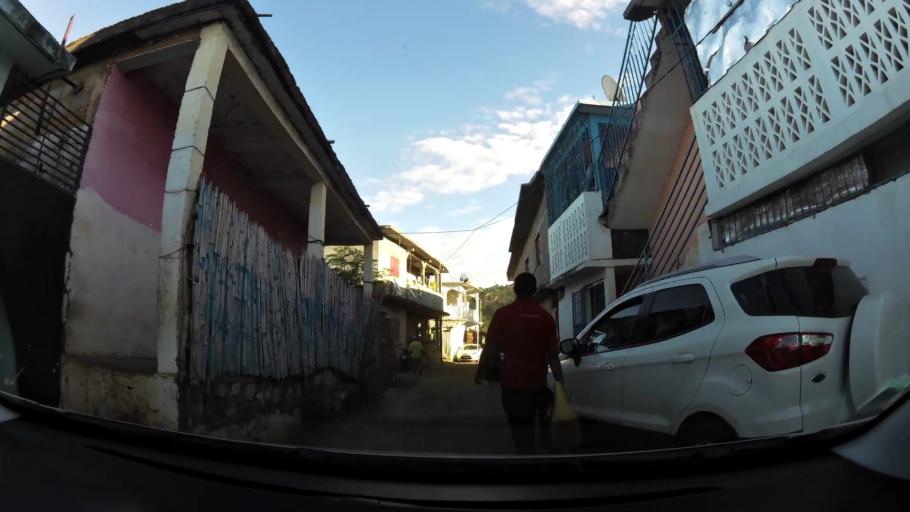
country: YT
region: Koungou
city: Koungou
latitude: -12.7351
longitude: 45.2056
